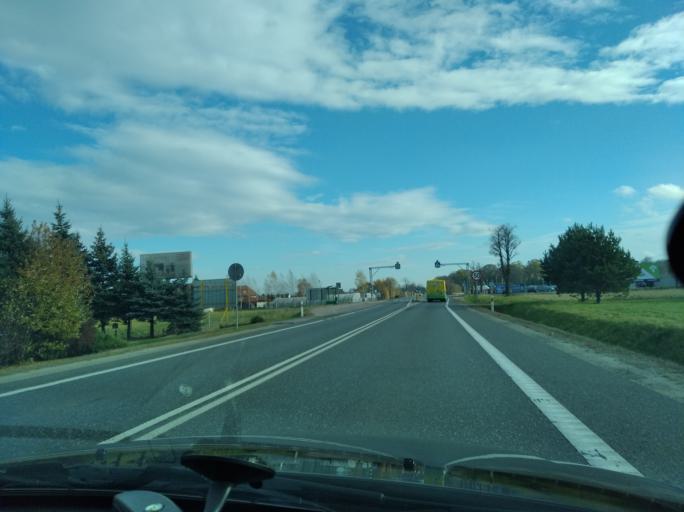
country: PL
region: Subcarpathian Voivodeship
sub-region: Powiat debicki
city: Brzeznica
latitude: 50.0584
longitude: 21.4695
